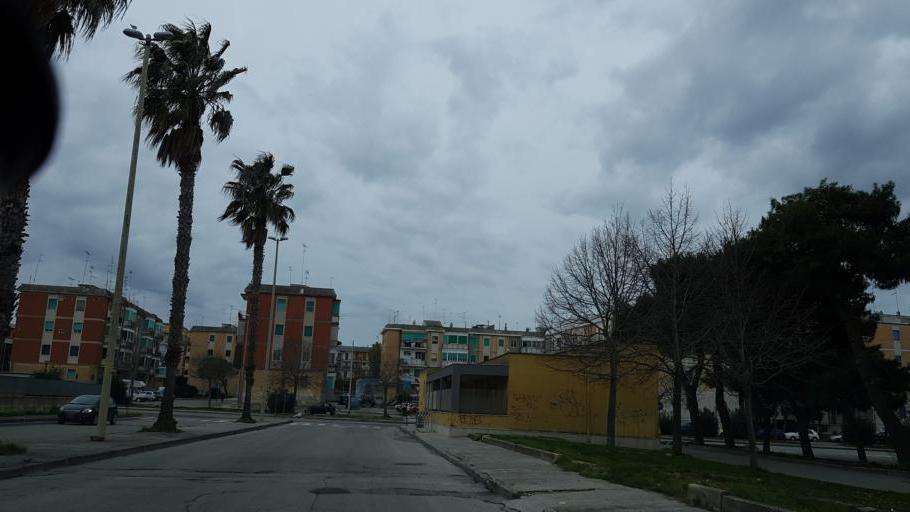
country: IT
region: Apulia
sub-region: Provincia di Brindisi
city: Brindisi
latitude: 40.6197
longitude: 17.9269
